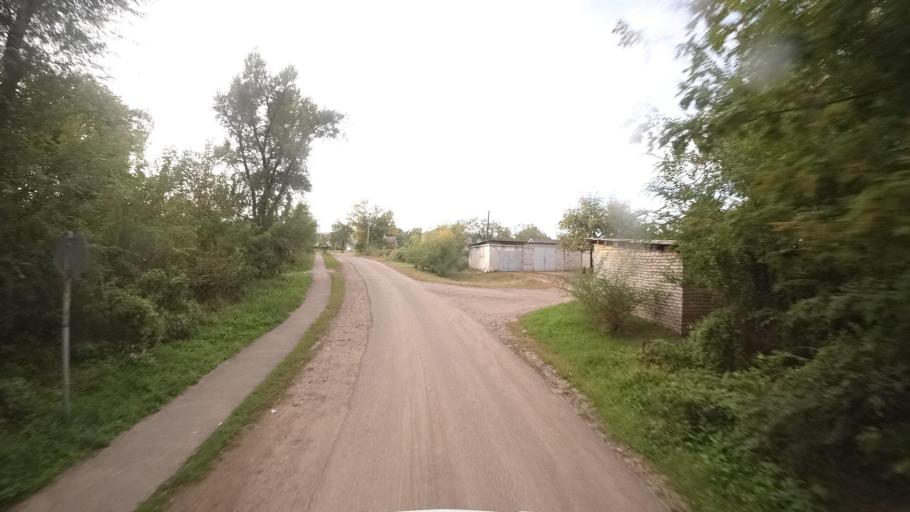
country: RU
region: Primorskiy
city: Yakovlevka
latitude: 44.4204
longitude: 133.4759
